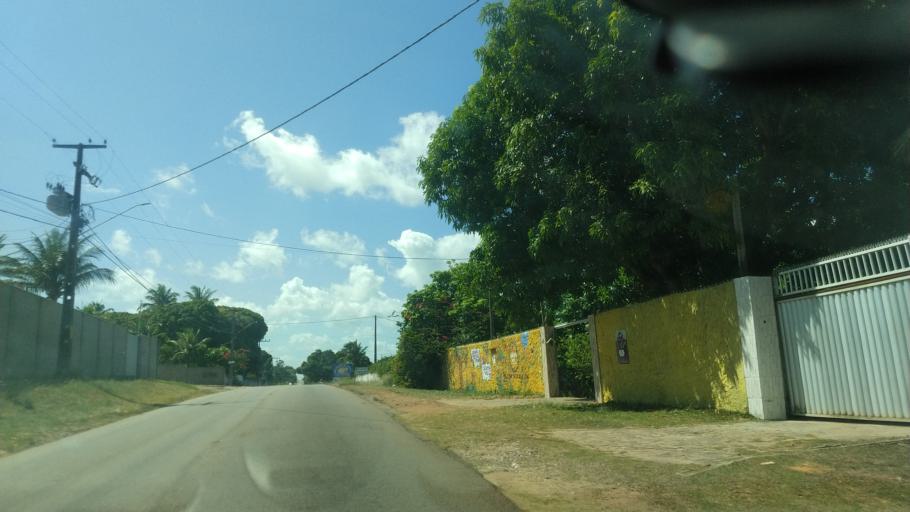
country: BR
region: Rio Grande do Norte
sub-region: Parnamirim
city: Parnamirim
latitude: -5.9497
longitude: -35.1794
